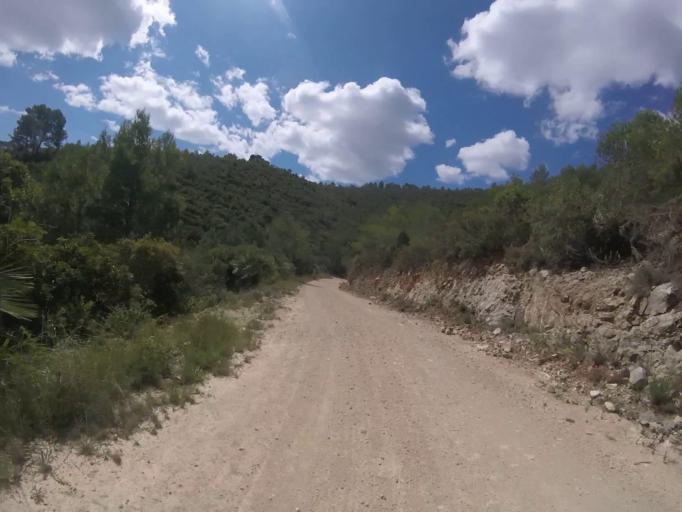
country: ES
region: Valencia
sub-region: Provincia de Castello
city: Santa Magdalena de Pulpis
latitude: 40.3095
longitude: 0.3199
